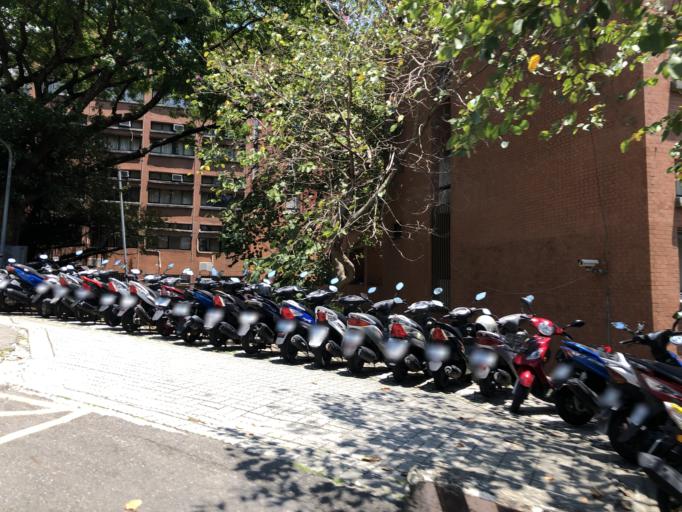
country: TW
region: Kaohsiung
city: Kaohsiung
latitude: 22.6288
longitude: 120.2676
